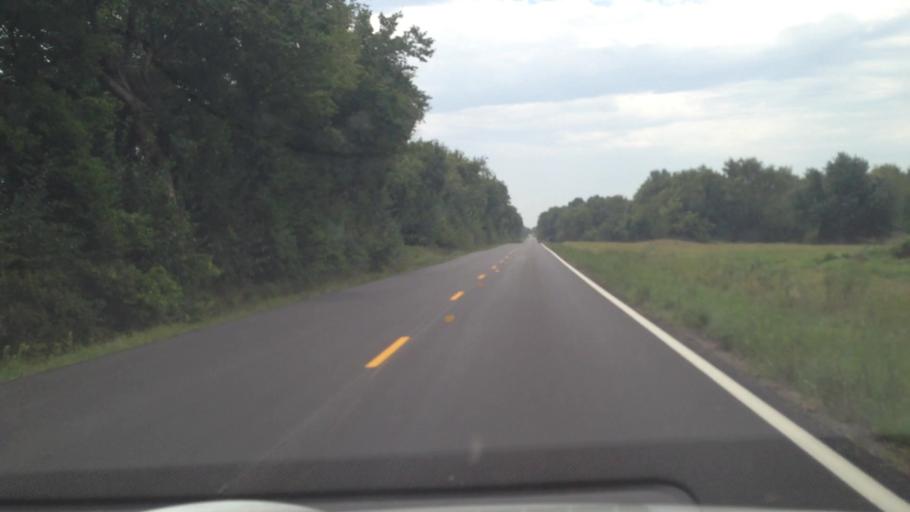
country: US
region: Kansas
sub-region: Crawford County
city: Girard
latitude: 37.5261
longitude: -94.9606
